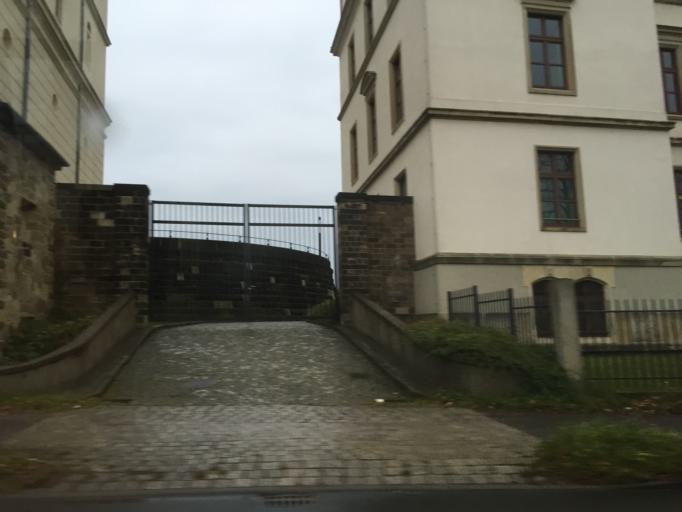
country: DE
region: Saxony
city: Albertstadt
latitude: 51.0785
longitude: 13.7578
